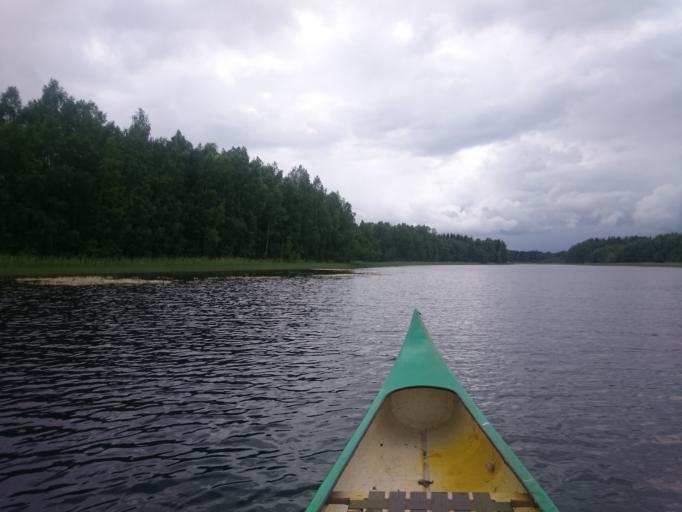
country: SE
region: Vaesternorrland
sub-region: OErnskoeldsviks Kommun
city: Ornskoldsvik
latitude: 63.6475
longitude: 18.6185
